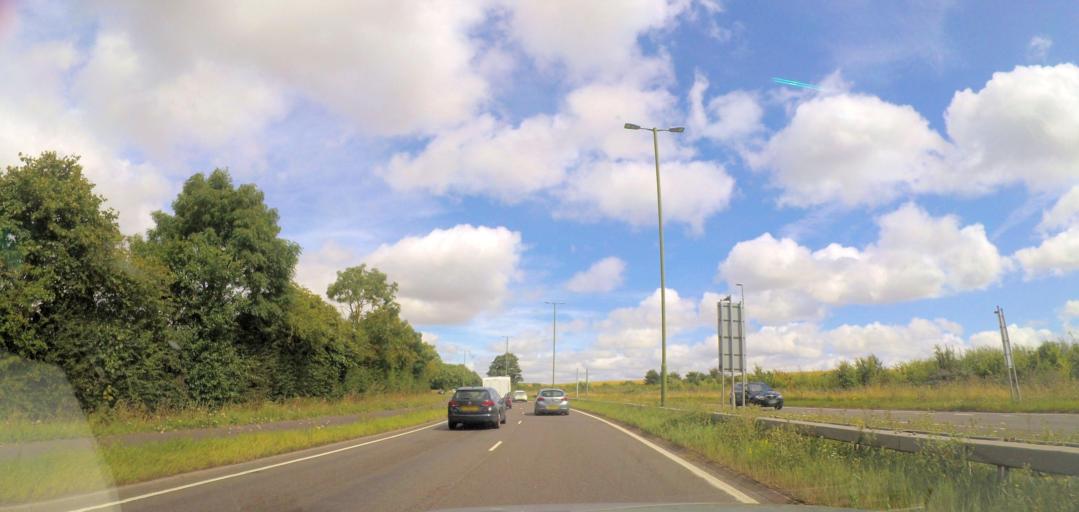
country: GB
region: England
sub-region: Hertfordshire
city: Baldock
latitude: 51.9624
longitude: -0.1993
